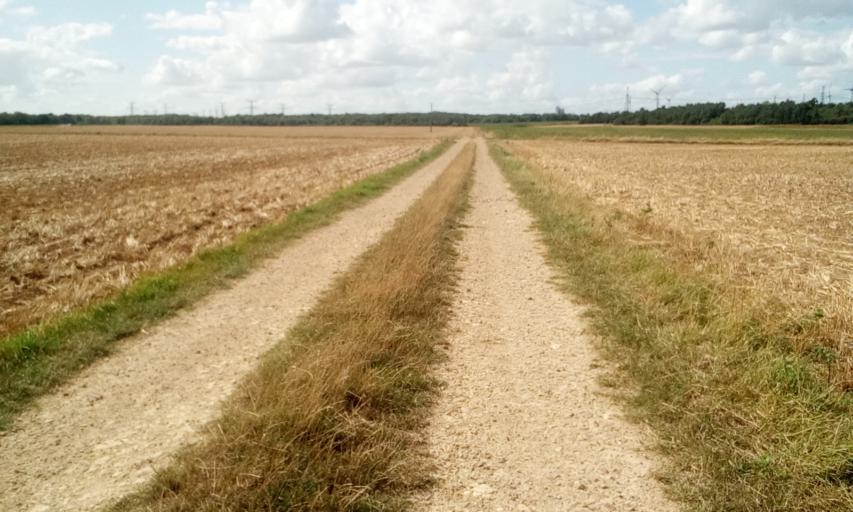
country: FR
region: Lower Normandy
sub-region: Departement du Calvados
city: Bellengreville
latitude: 49.1095
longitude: -0.2294
